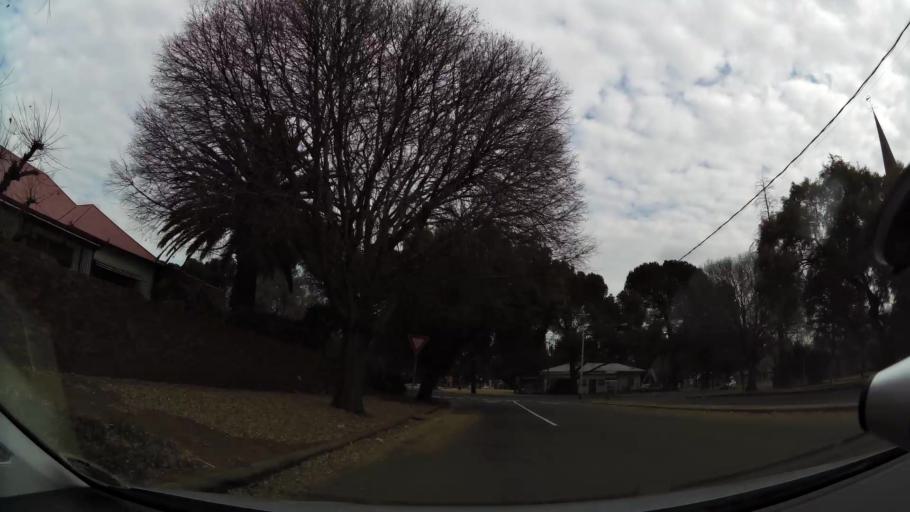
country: ZA
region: Orange Free State
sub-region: Mangaung Metropolitan Municipality
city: Bloemfontein
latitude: -29.1025
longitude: 26.2081
